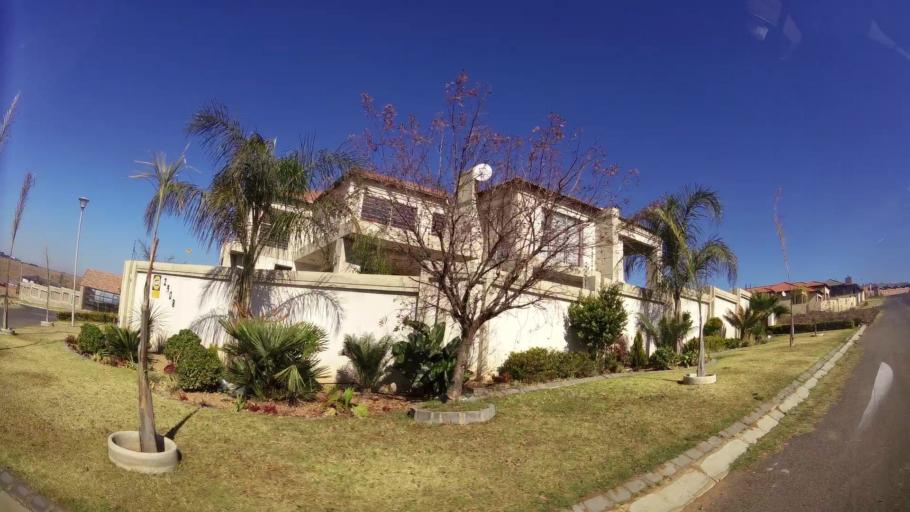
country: ZA
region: Mpumalanga
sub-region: Nkangala District Municipality
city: Witbank
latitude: -25.8673
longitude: 29.2574
